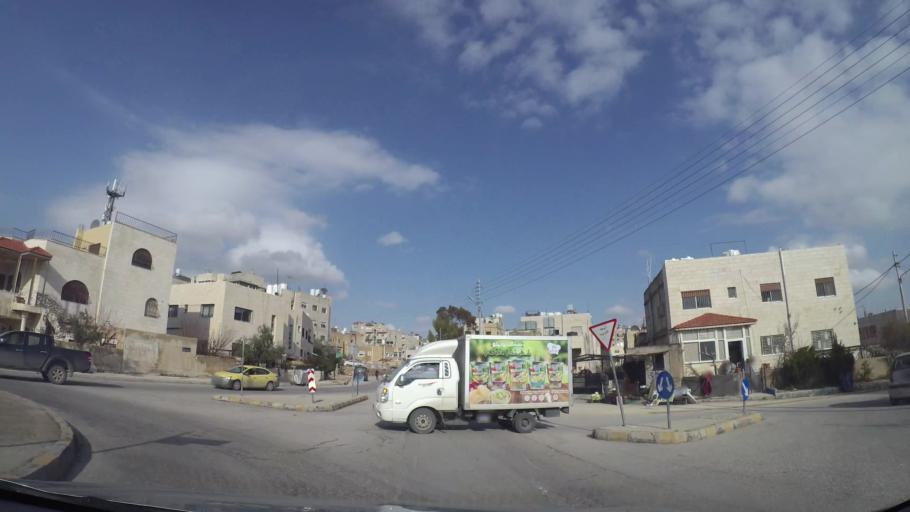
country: JO
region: Amman
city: Al Jubayhah
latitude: 32.0190
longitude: 35.8490
